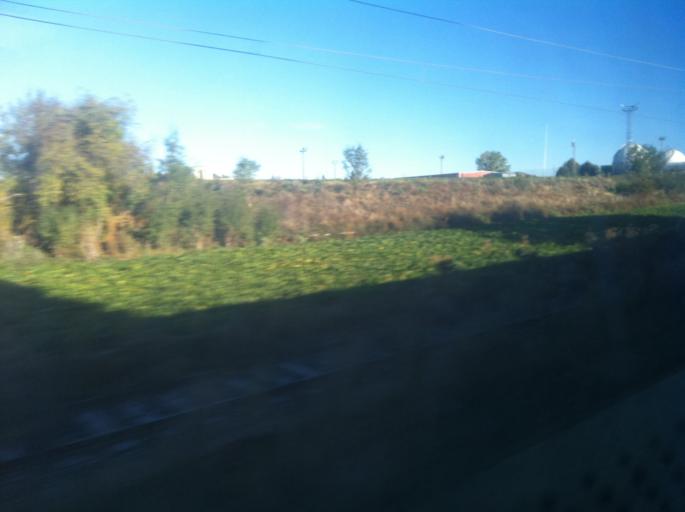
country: ES
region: Castille and Leon
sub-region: Provincia de Palencia
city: Soto de Cerrato
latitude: 41.9546
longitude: -4.4504
